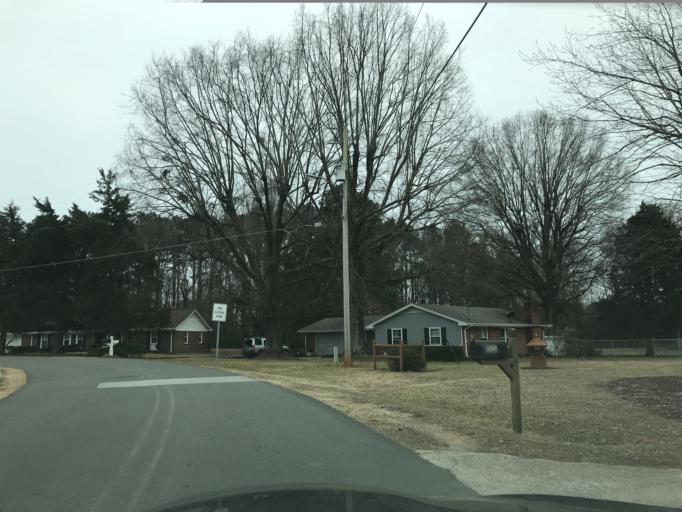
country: US
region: North Carolina
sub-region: Wake County
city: Raleigh
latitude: 35.8654
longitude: -78.6002
